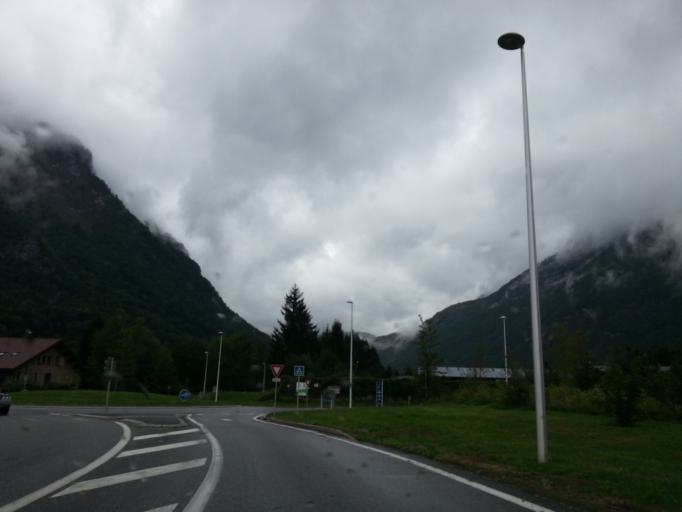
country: FR
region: Rhone-Alpes
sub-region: Departement de la Savoie
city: Ugine
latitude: 45.7570
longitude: 6.3995
